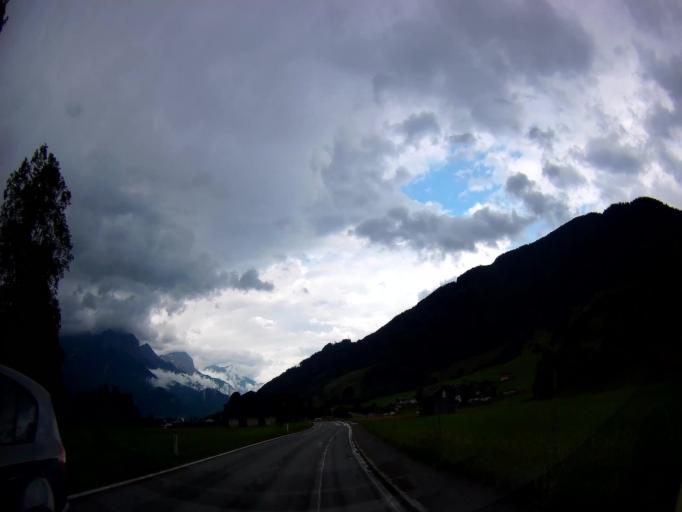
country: AT
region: Salzburg
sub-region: Politischer Bezirk Zell am See
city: Leogang
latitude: 47.4401
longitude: 12.7690
